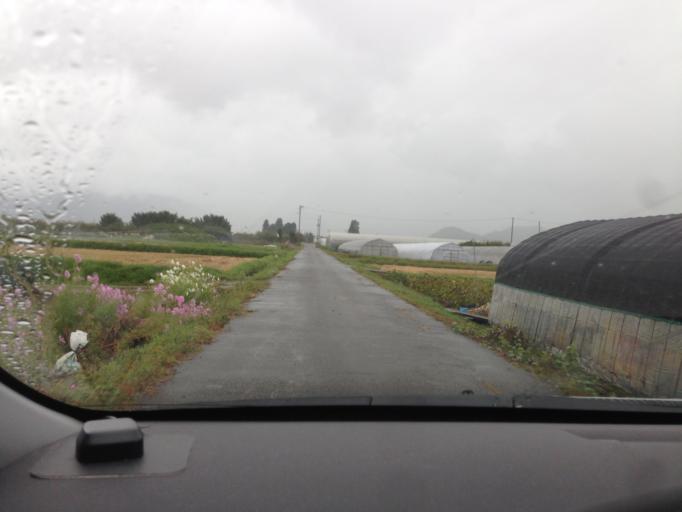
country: JP
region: Fukushima
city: Kitakata
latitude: 37.4639
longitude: 139.8658
